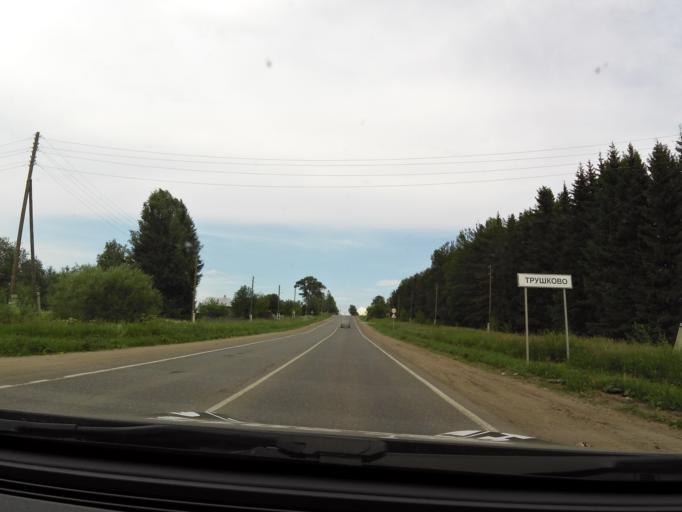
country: RU
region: Kirov
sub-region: Kirovo-Chepetskiy Rayon
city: Kirov
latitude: 58.6278
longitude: 49.8050
